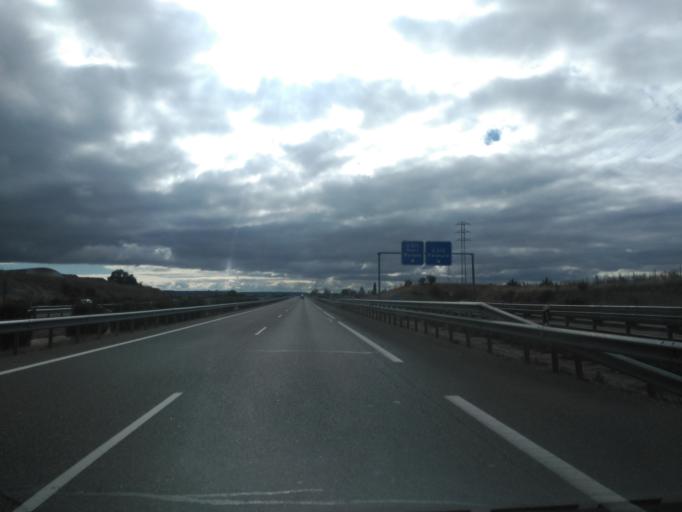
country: ES
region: Castille and Leon
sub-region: Provincia de Palencia
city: Palencia
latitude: 41.9858
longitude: -4.5023
